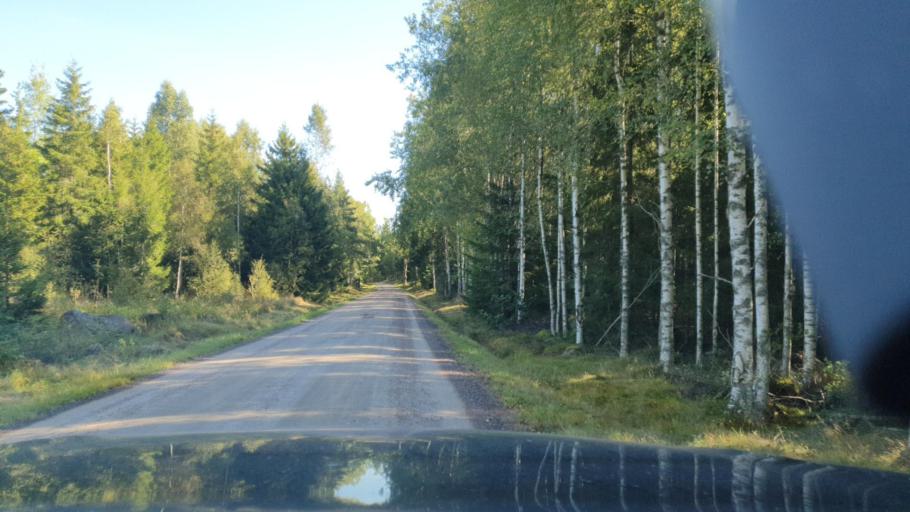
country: SE
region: Vaermland
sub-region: Kristinehamns Kommun
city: Bjorneborg
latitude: 59.2090
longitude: 14.2296
